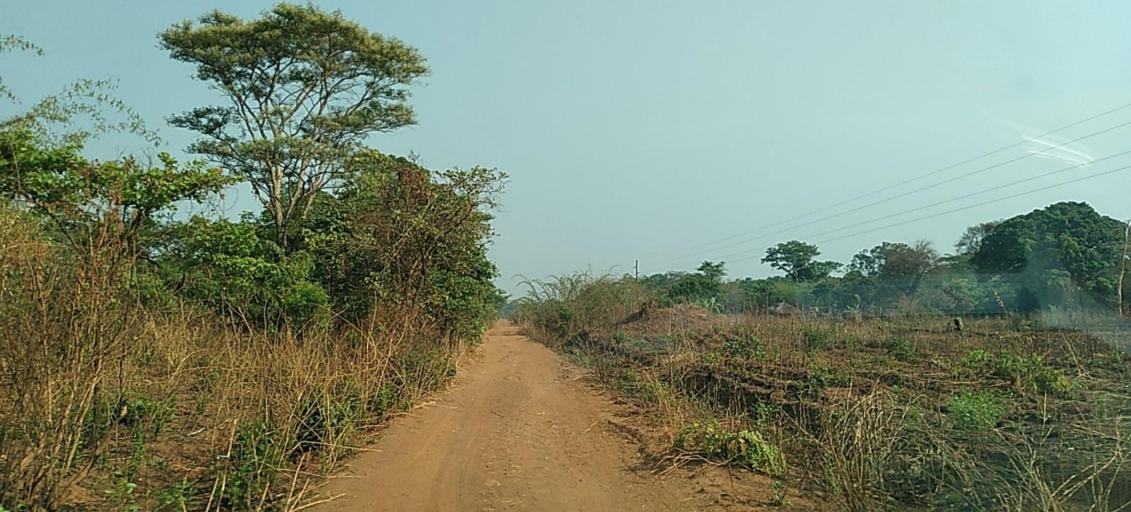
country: ZM
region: Copperbelt
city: Chingola
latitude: -12.8475
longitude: 27.5496
